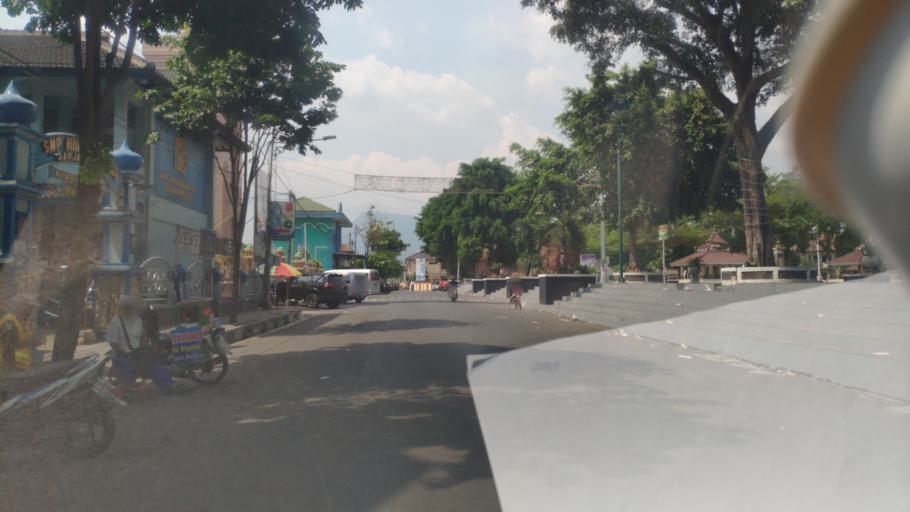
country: ID
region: Central Java
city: Wonosobo
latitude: -7.3967
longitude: 109.6944
